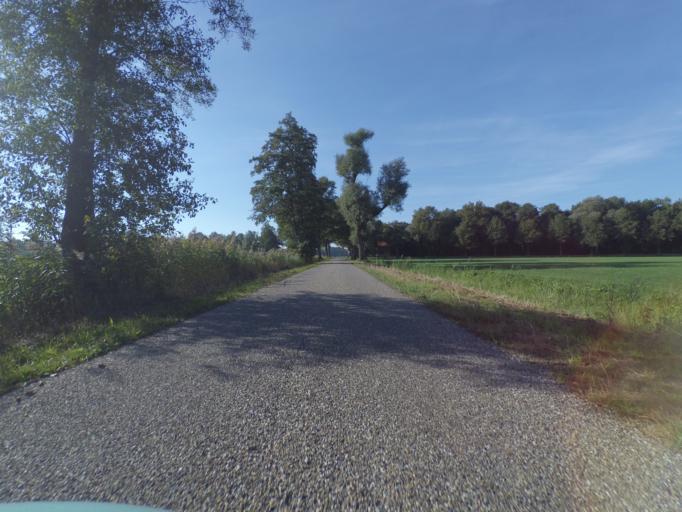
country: NL
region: Gelderland
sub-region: Berkelland
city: Borculo
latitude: 52.0769
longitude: 6.5477
